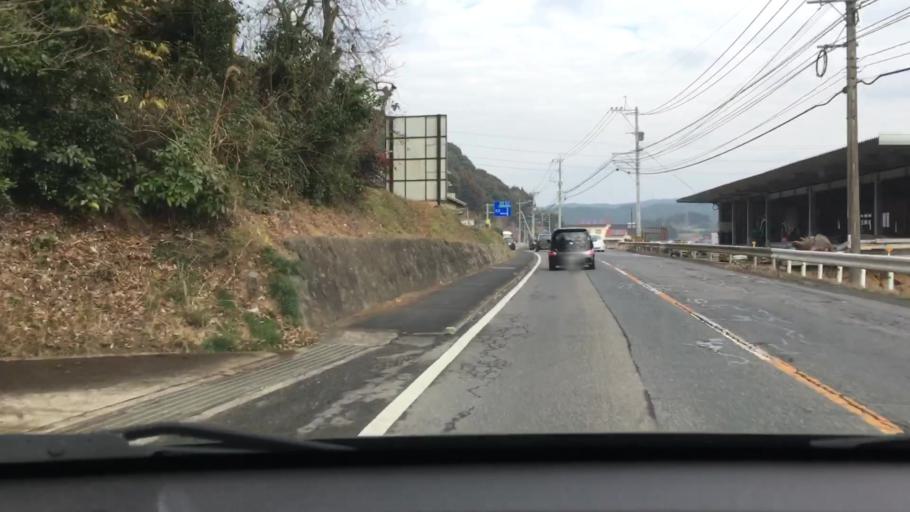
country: JP
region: Saga Prefecture
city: Imaricho-ko
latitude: 33.3026
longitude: 129.9207
